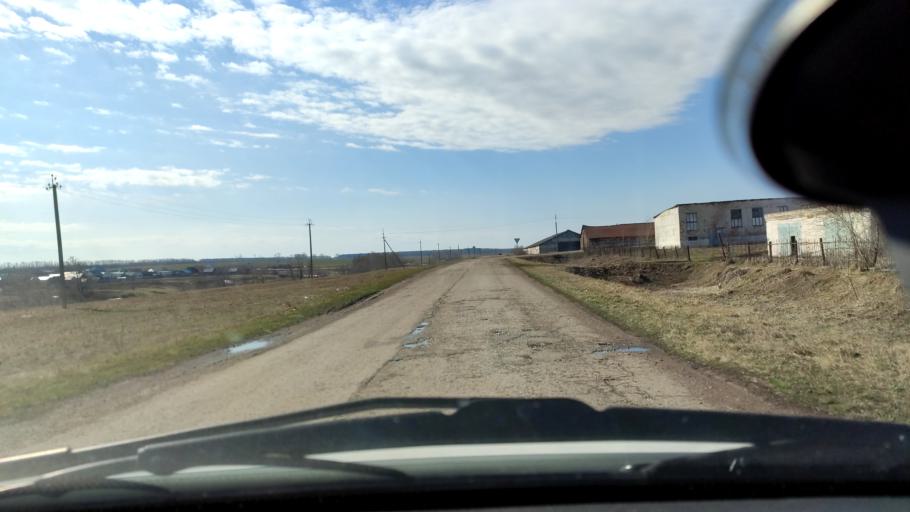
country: RU
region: Bashkortostan
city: Tolbazy
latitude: 54.1700
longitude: 55.9464
